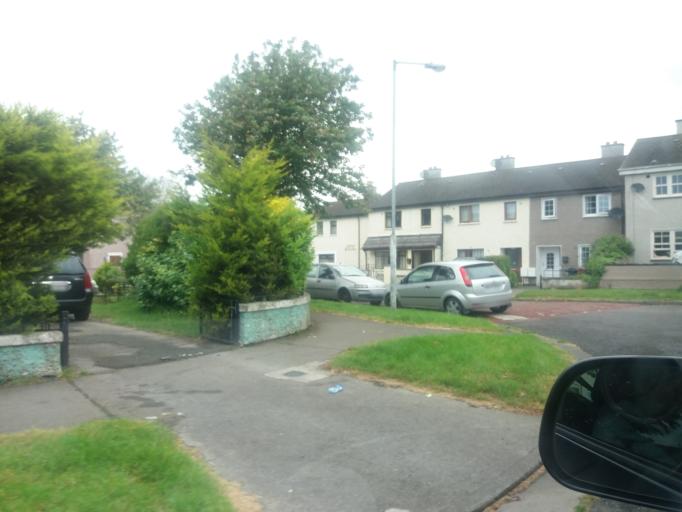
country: IE
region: Leinster
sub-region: Fingal County
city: Blanchardstown
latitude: 53.4049
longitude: -6.3877
